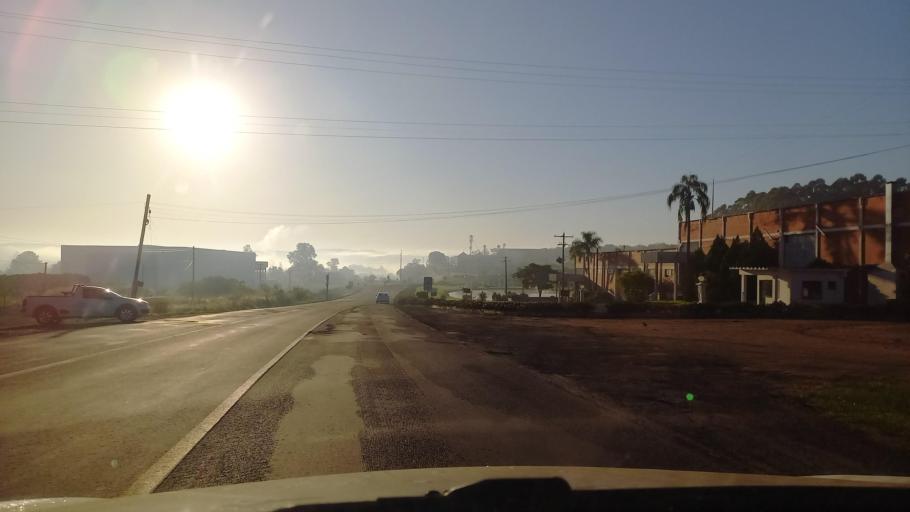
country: BR
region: Rio Grande do Sul
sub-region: Santa Cruz Do Sul
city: Santa Cruz do Sul
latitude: -29.6946
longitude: -52.5035
